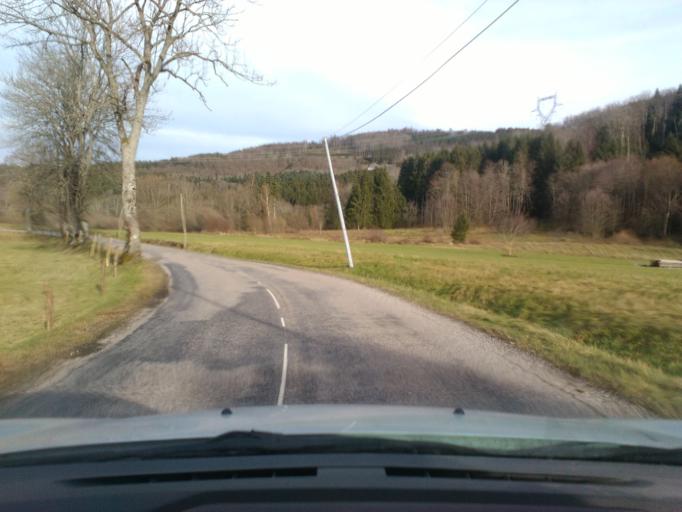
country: FR
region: Lorraine
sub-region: Departement des Vosges
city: Plainfaing
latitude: 48.1505
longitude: 6.9839
